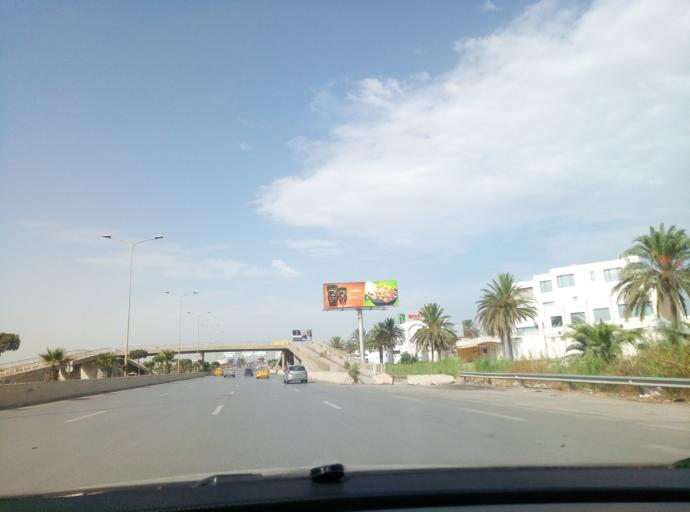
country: TN
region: Ariana
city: Ariana
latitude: 36.8288
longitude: 10.2060
